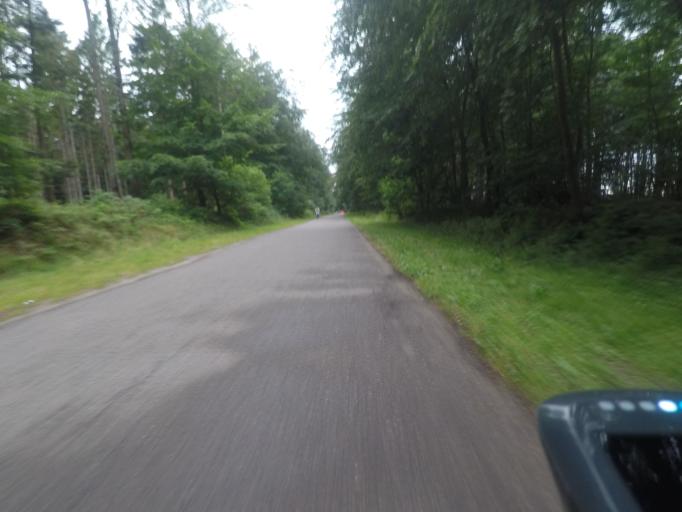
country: DE
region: Mecklenburg-Vorpommern
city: Ostseebad Kuhlungsborn
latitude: 54.1440
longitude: 11.8317
